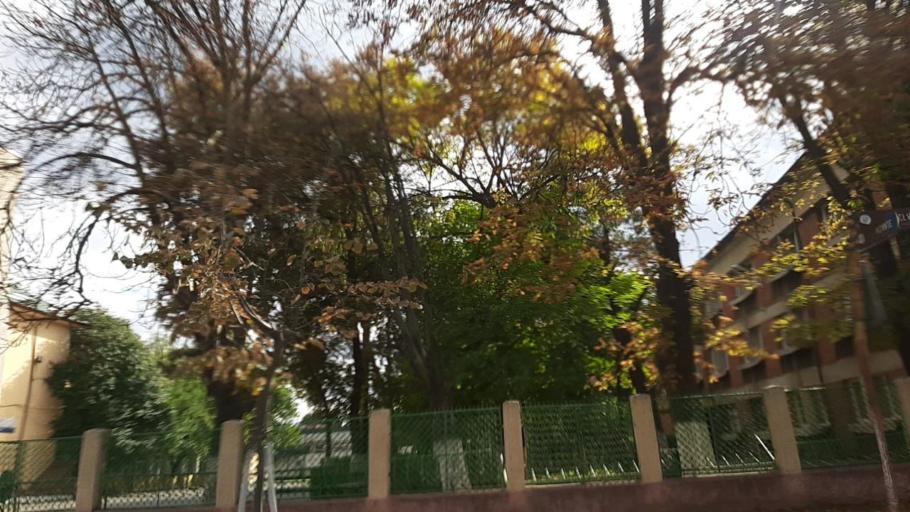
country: RO
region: Galati
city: Galati
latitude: 45.4484
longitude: 28.0343
